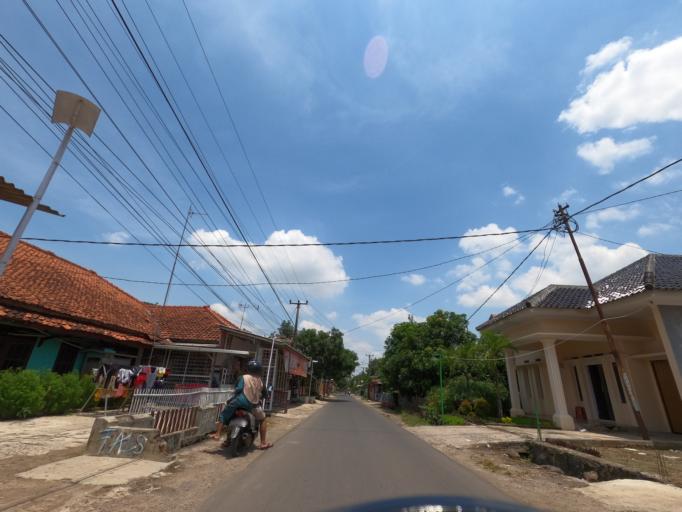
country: ID
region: West Java
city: Pamanukan
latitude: -6.5355
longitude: 107.7706
